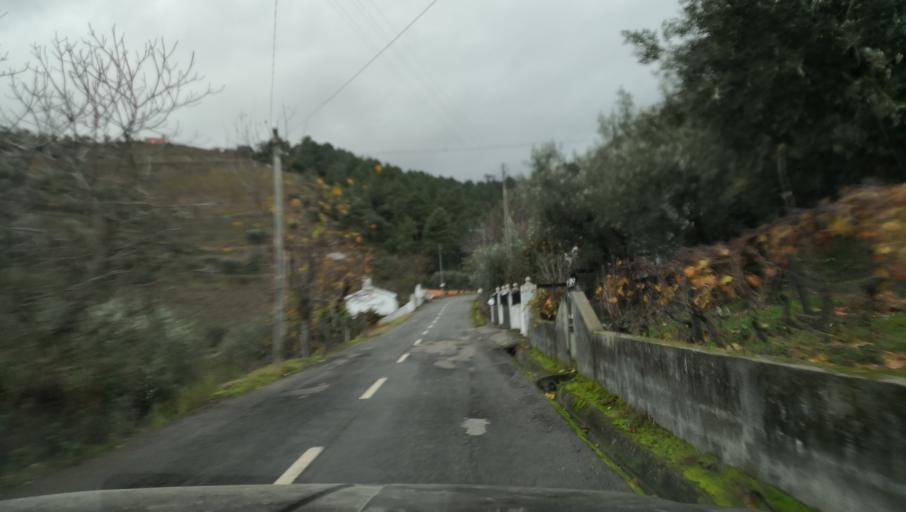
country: PT
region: Vila Real
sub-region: Vila Real
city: Vila Real
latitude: 41.2426
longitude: -7.7390
